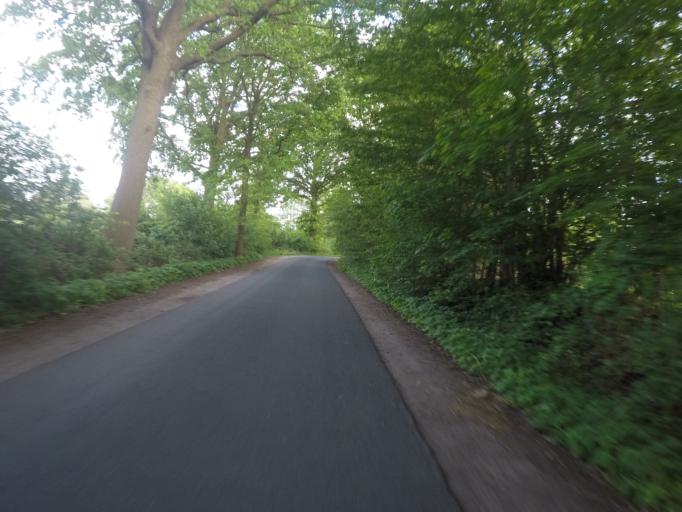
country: DE
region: Schleswig-Holstein
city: Bonningstedt
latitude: 53.6613
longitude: 9.9254
